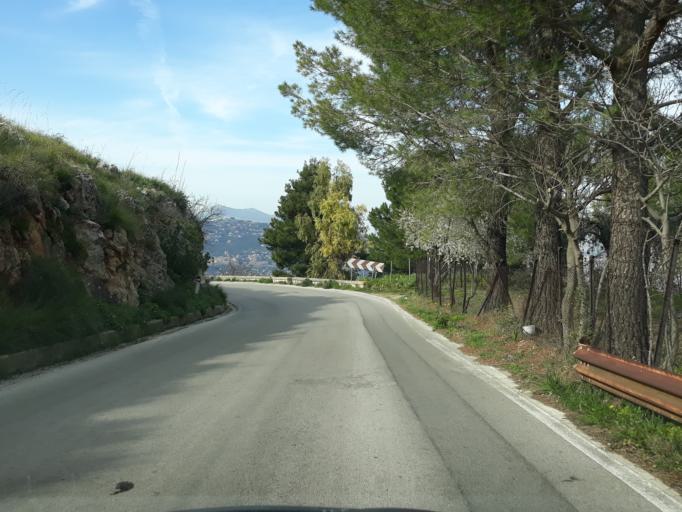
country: IT
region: Sicily
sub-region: Palermo
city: Piano Maglio-Blandino
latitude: 38.0435
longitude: 13.3101
